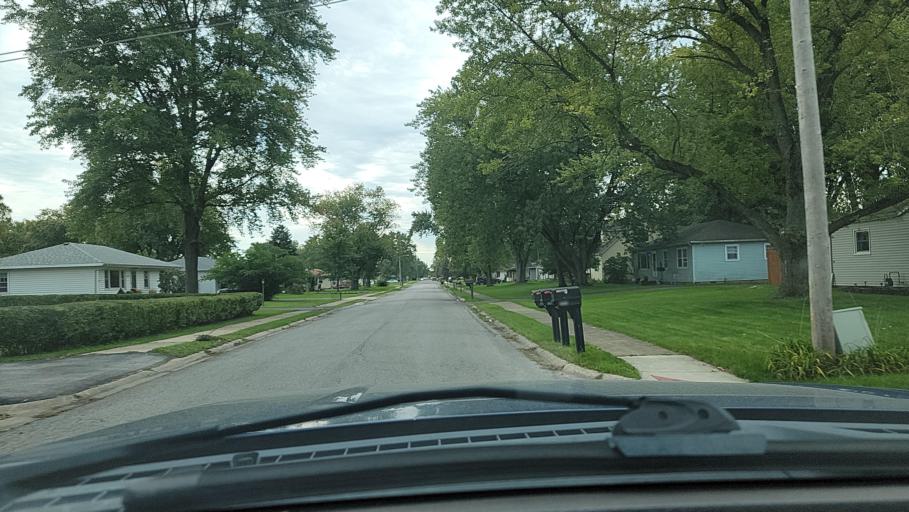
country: US
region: Indiana
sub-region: Lake County
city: Lake Station
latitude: 41.5633
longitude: -87.2138
